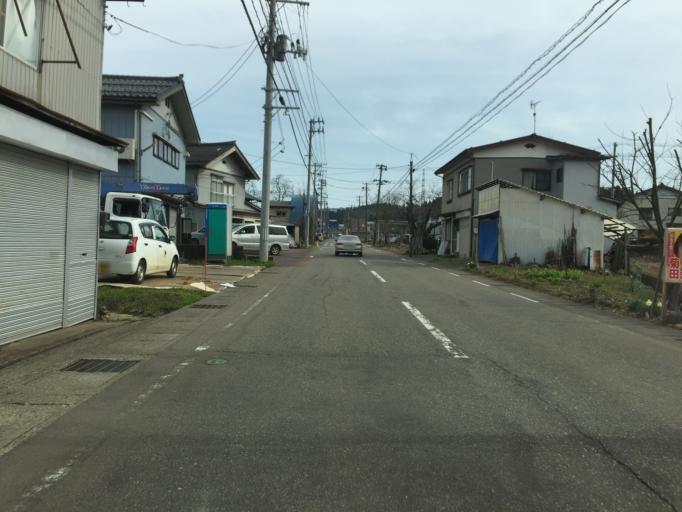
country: JP
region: Niigata
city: Tochio-honcho
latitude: 37.4641
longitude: 139.0049
